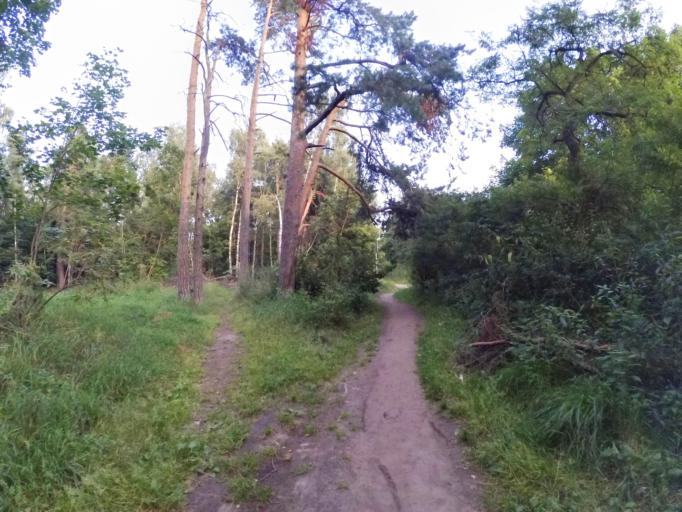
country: RU
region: Moscow
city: Kuz'minki
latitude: 55.6903
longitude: 37.8033
